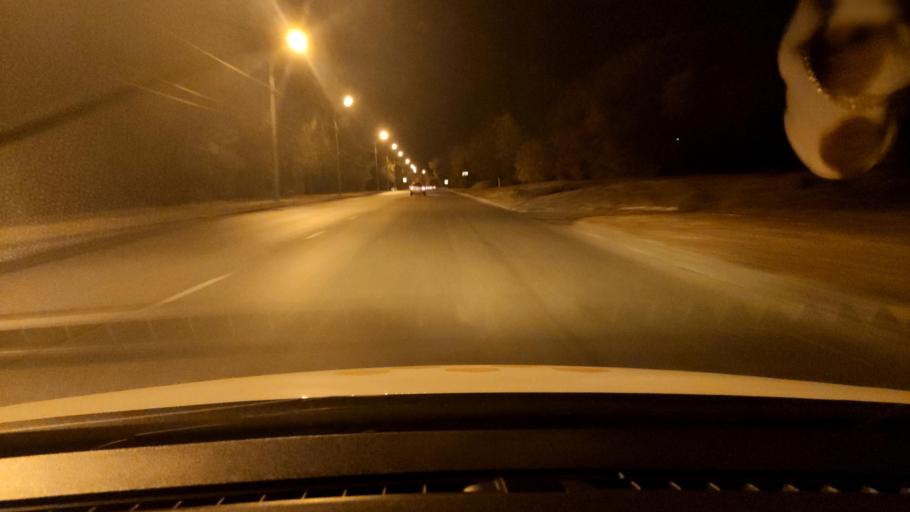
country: RU
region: Voronezj
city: Voronezh
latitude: 51.6436
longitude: 39.2109
